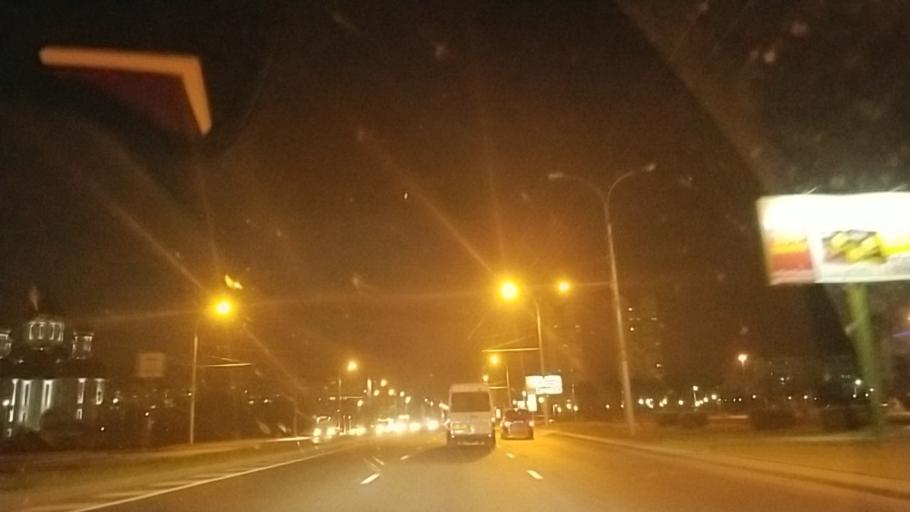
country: BY
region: Brest
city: Brest
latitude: 52.0968
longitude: 23.7655
